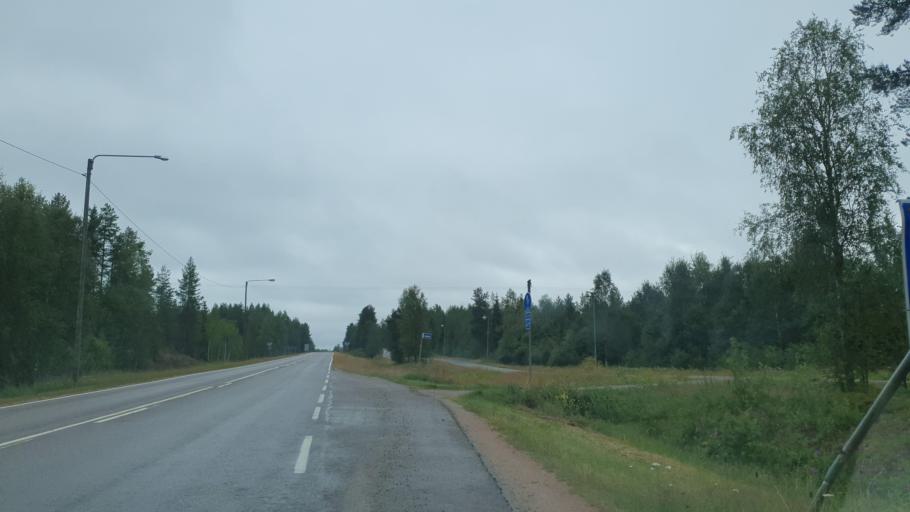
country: FI
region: Lapland
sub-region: Itae-Lappi
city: Kemijaervi
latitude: 66.7212
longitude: 27.3656
